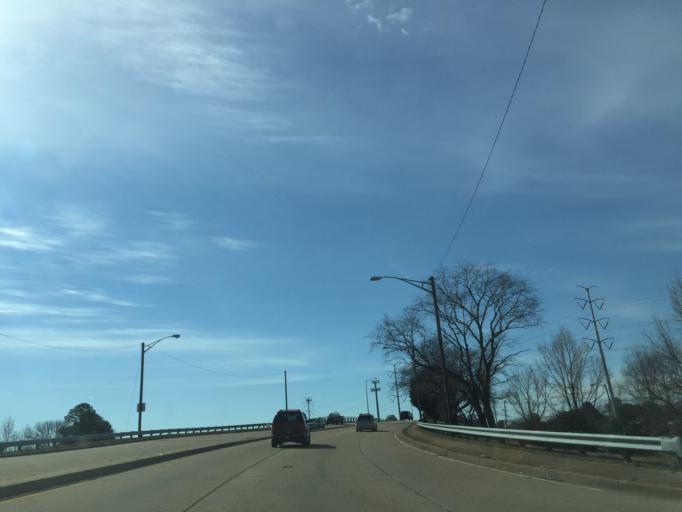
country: US
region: Virginia
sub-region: City of Norfolk
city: Norfolk
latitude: 36.8989
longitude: -76.2558
